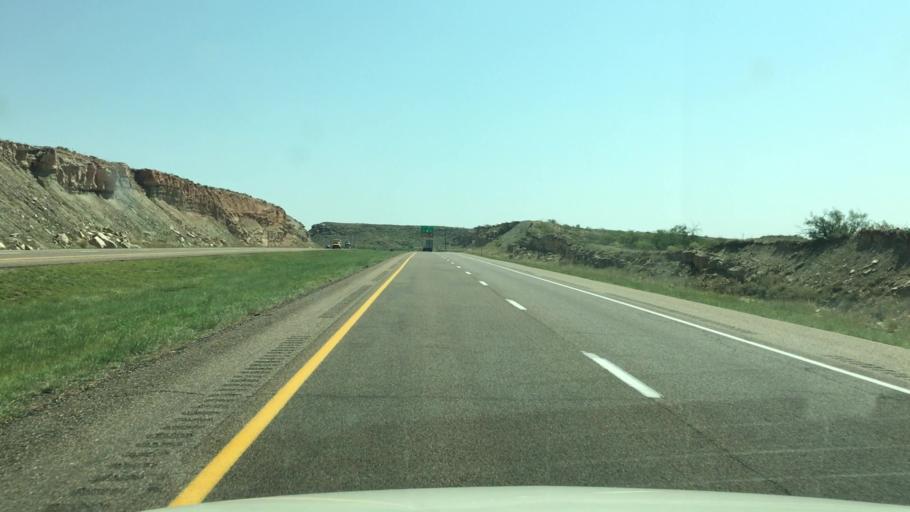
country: US
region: New Mexico
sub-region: Quay County
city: Tucumcari
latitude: 35.1486
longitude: -103.7864
